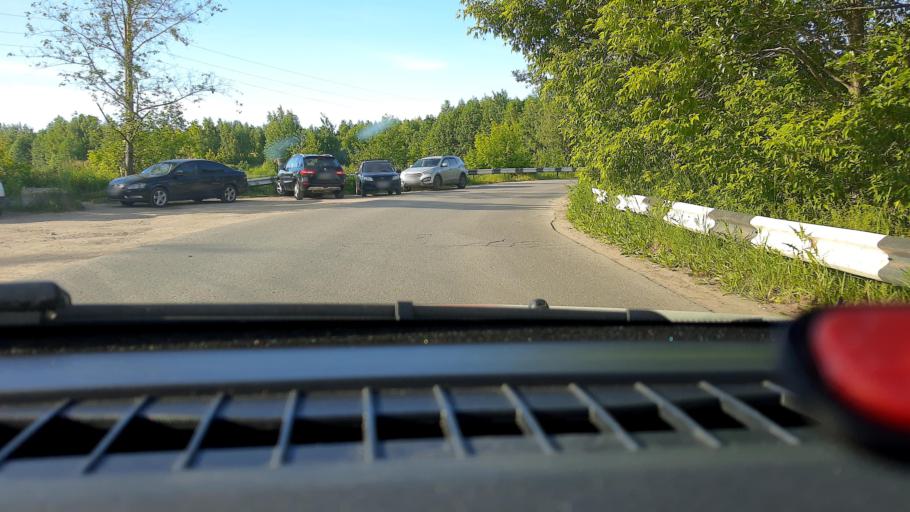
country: RU
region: Nizjnij Novgorod
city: Gorbatovka
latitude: 56.2227
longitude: 43.7548
